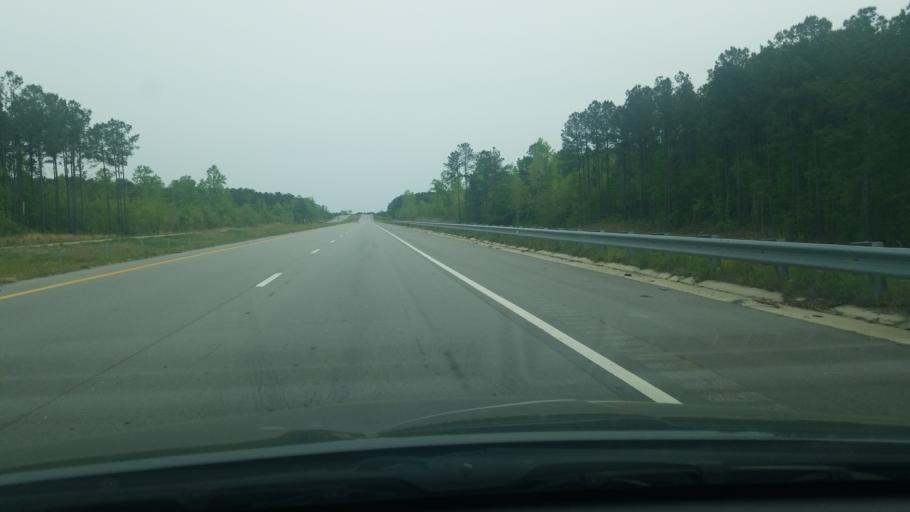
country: US
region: North Carolina
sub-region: Craven County
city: River Bend
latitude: 35.0200
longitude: -77.2271
